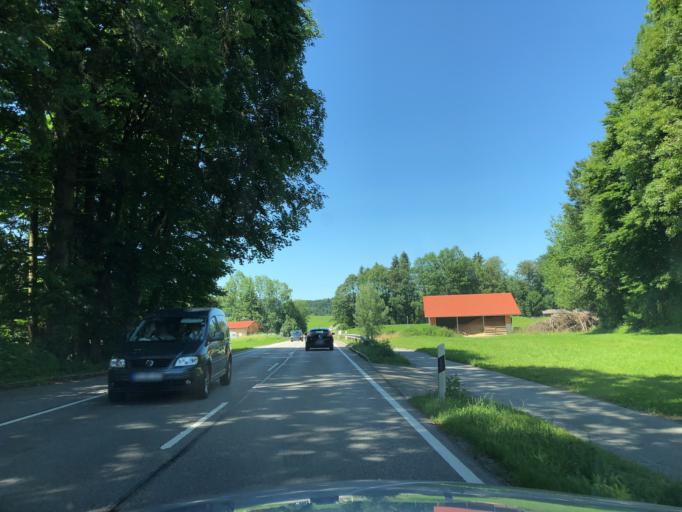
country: DE
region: Bavaria
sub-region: Upper Bavaria
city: Frasdorf
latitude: 47.7959
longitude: 12.2979
